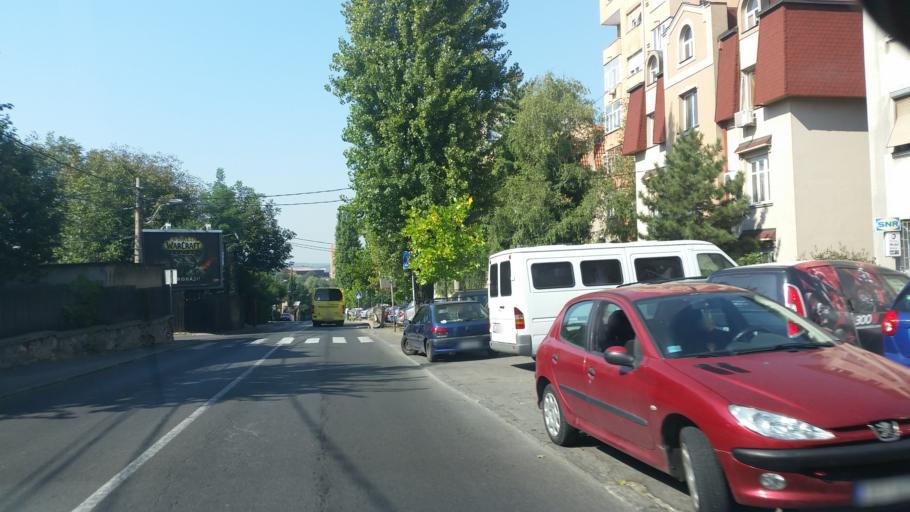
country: RS
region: Central Serbia
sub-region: Belgrade
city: Palilula
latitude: 44.7923
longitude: 20.5020
